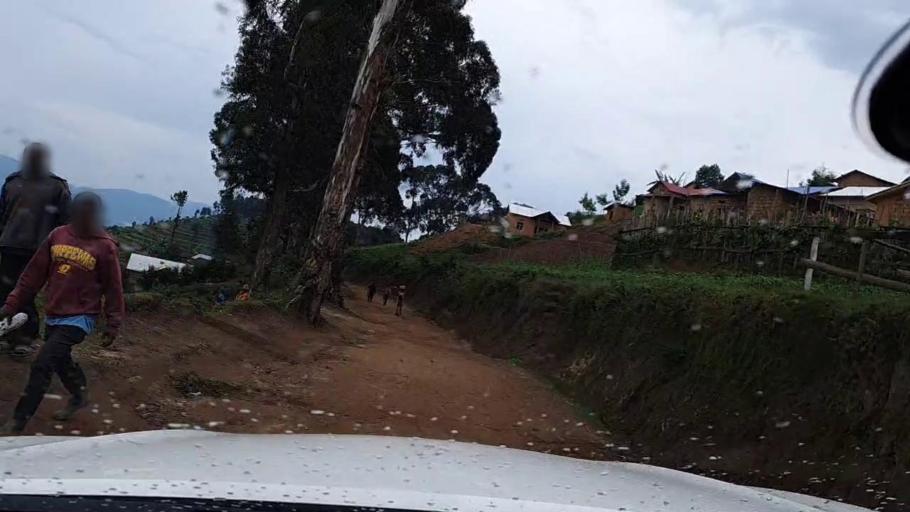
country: RW
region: Southern Province
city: Nzega
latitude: -2.3781
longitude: 29.2474
